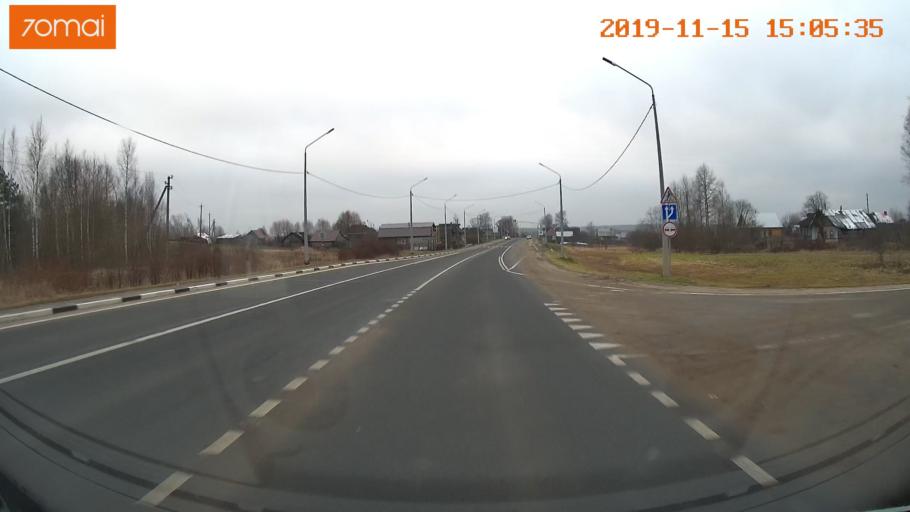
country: RU
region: Jaroslavl
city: Prechistoye
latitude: 58.4019
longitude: 40.3224
